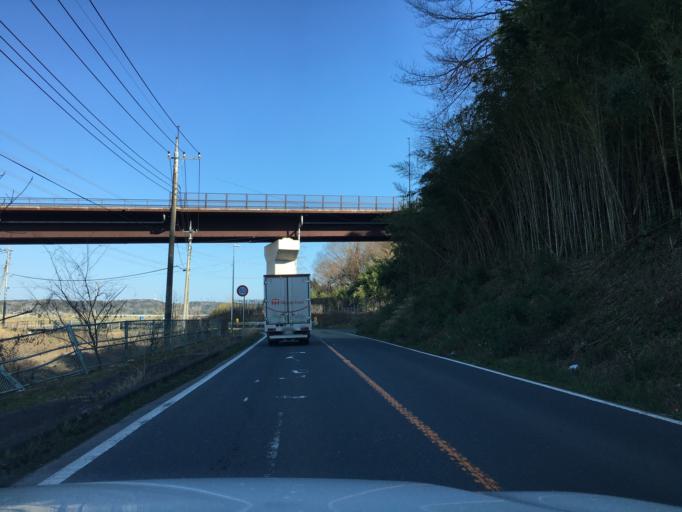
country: JP
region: Ibaraki
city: Omiya
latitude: 36.4869
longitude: 140.3798
